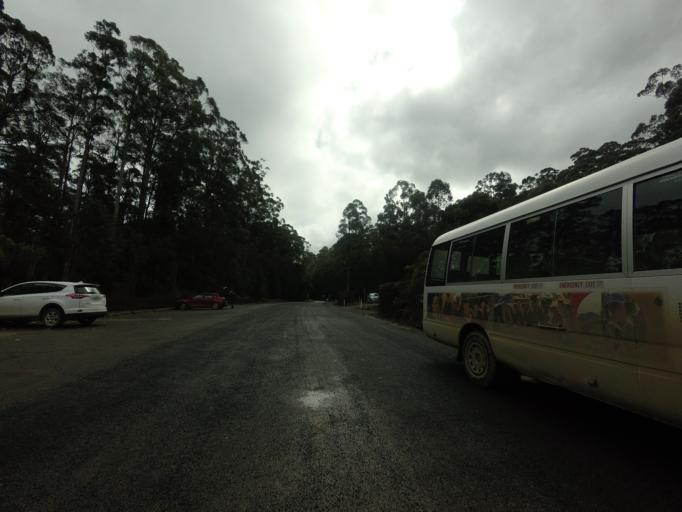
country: AU
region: Tasmania
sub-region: Huon Valley
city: Geeveston
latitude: -43.4129
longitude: 146.8740
